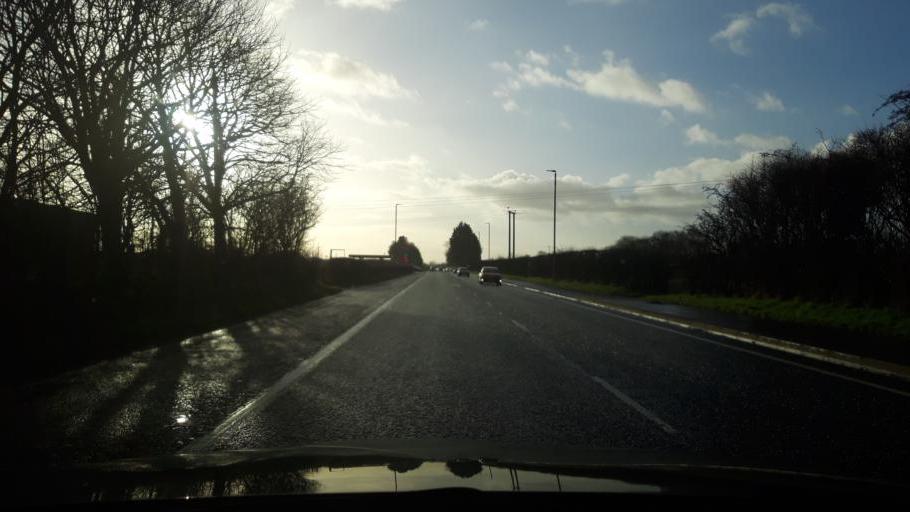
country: GB
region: Northern Ireland
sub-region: Coleraine District
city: Coleraine
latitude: 55.1120
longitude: -6.6894
